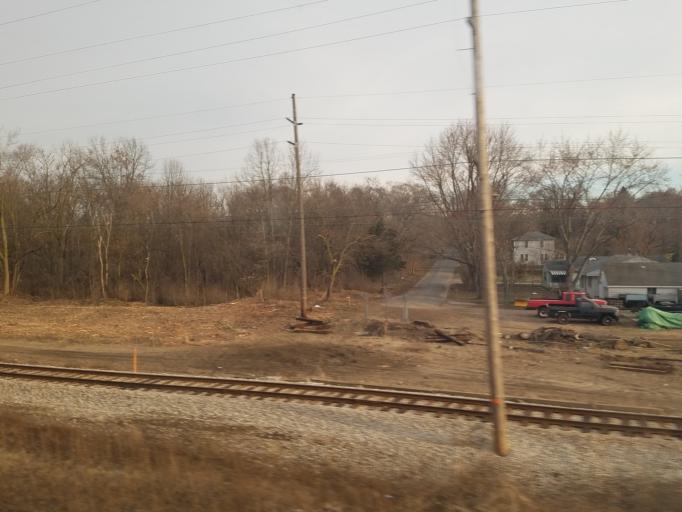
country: US
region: Indiana
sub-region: Saint Joseph County
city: South Bend
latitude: 41.6834
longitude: -86.3112
